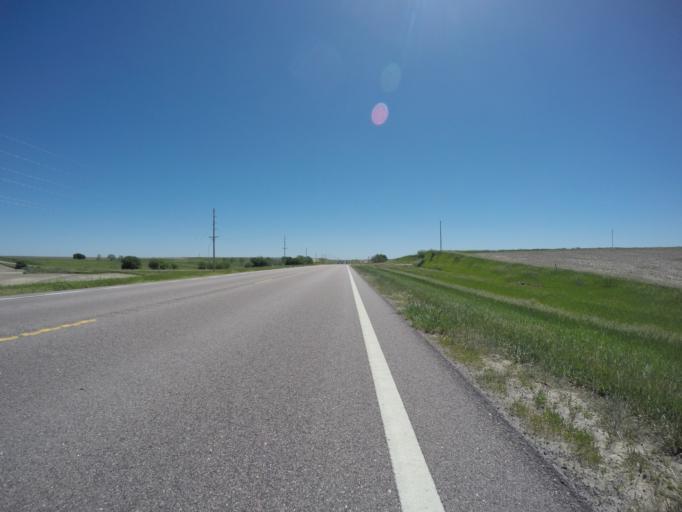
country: US
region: Kansas
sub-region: Norton County
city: Norton
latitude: 39.8284
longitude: -99.6283
